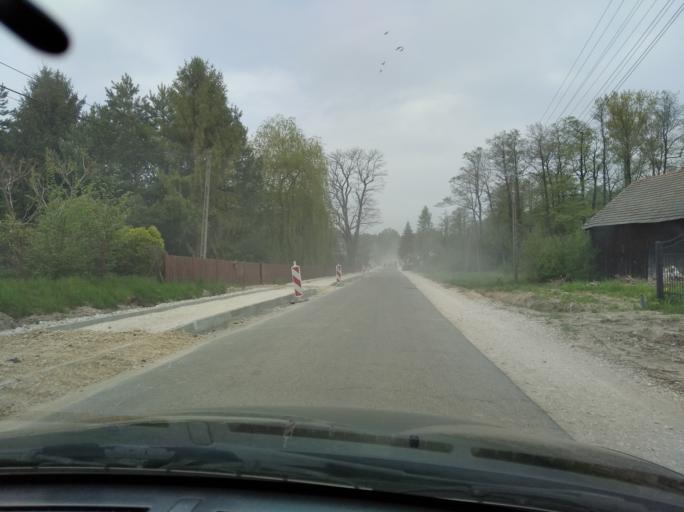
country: PL
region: Lesser Poland Voivodeship
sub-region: Powiat tarnowski
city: Skrzyszow
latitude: 49.9814
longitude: 21.0644
